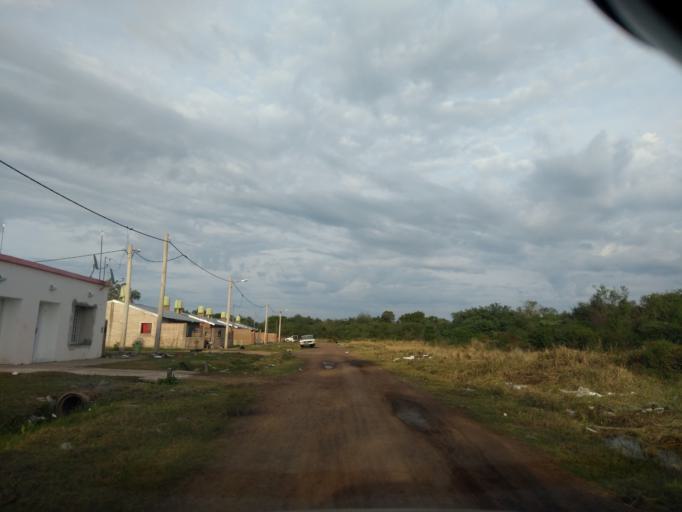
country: AR
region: Chaco
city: Fontana
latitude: -27.4231
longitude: -59.0495
